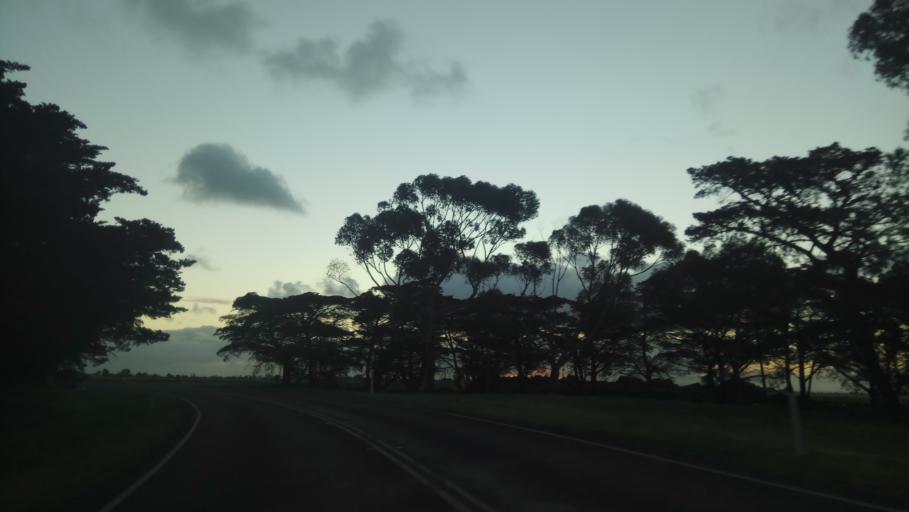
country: AU
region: Victoria
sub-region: Wyndham
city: Point Cook
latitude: -37.9229
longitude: 144.7445
